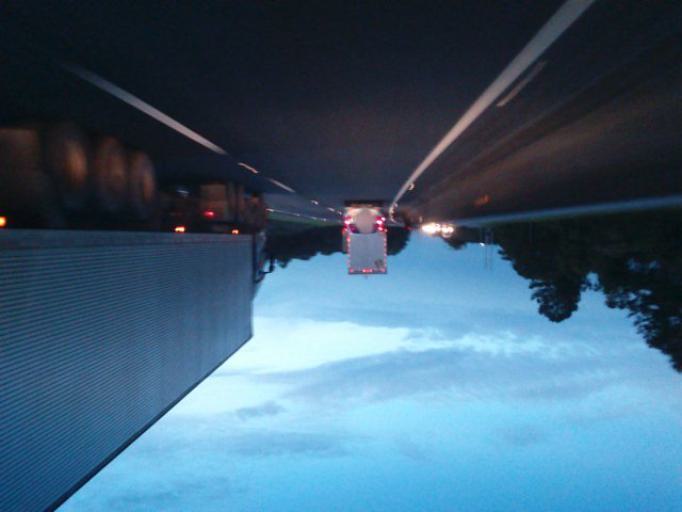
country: BR
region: Santa Catarina
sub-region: Barra Velha
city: Barra Velha
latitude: -26.4948
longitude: -48.7329
